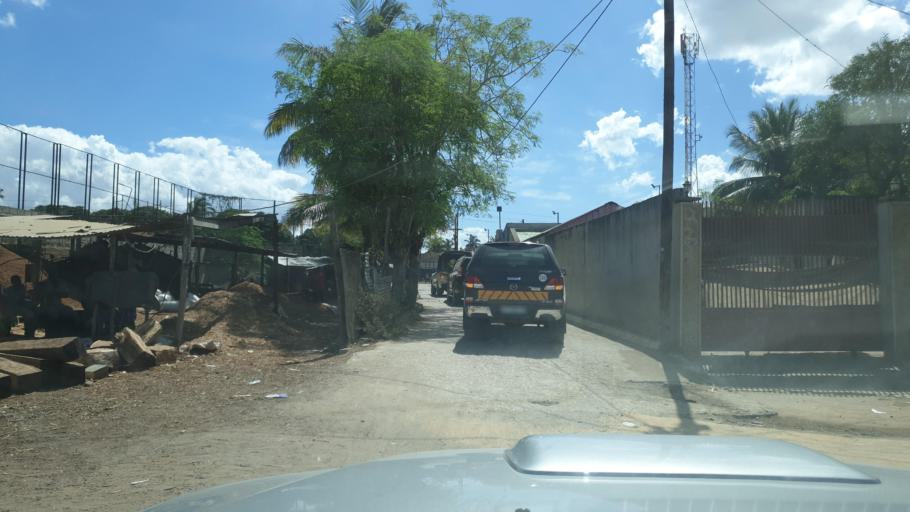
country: MZ
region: Nampula
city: Nacala
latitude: -14.5708
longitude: 40.6863
